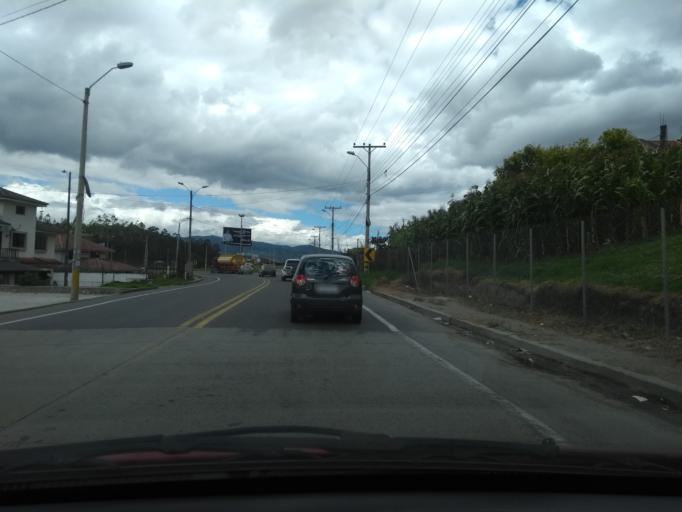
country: EC
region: Azuay
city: Cuenca
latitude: -3.0184
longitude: -79.0406
